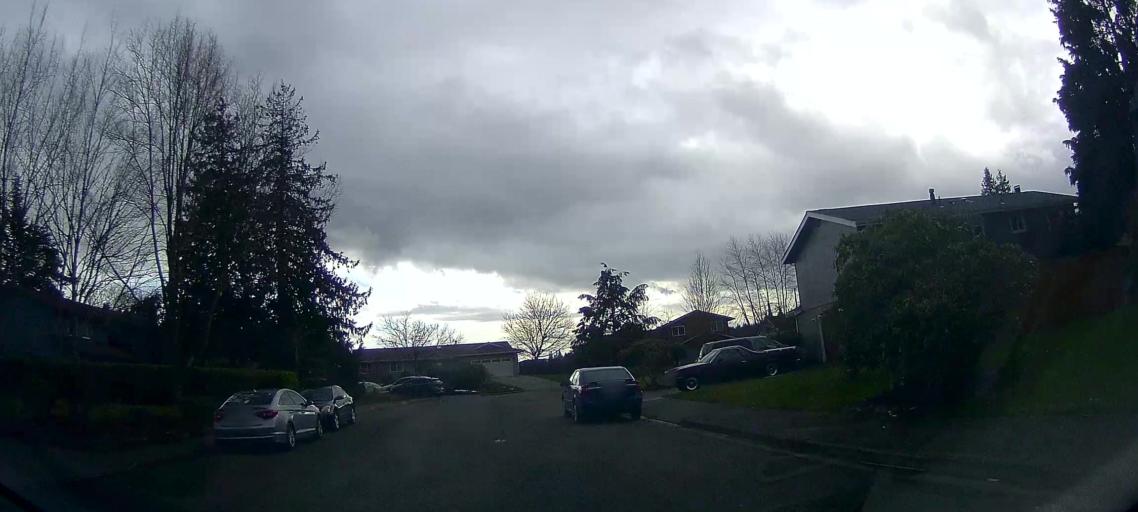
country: US
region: Washington
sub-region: Skagit County
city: Mount Vernon
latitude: 48.4402
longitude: -122.3163
